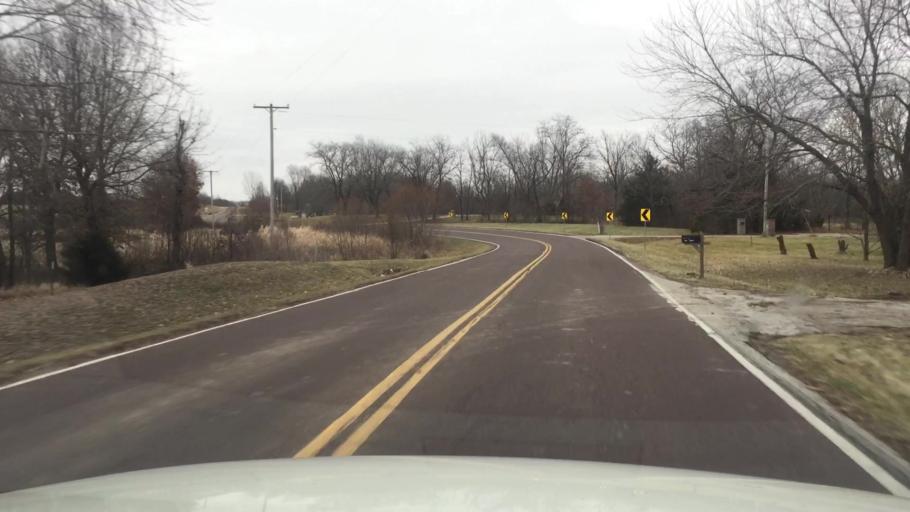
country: US
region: Missouri
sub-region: Boone County
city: Columbia
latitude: 38.8692
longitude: -92.2910
